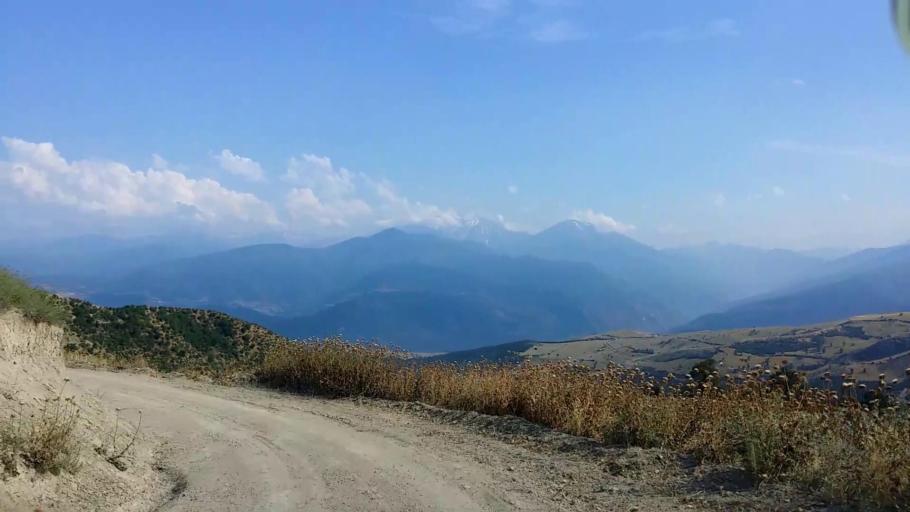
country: IR
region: Mazandaran
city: Chalus
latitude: 36.5472
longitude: 51.2967
